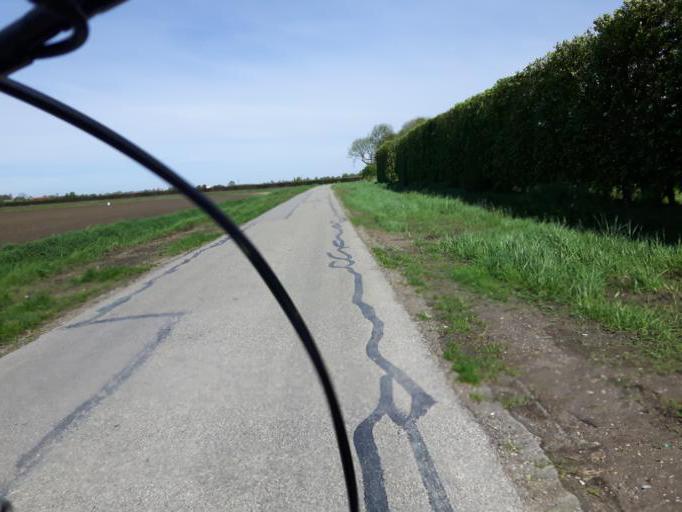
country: NL
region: Zeeland
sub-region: Gemeente Goes
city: Goes
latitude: 51.4551
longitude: 3.8764
